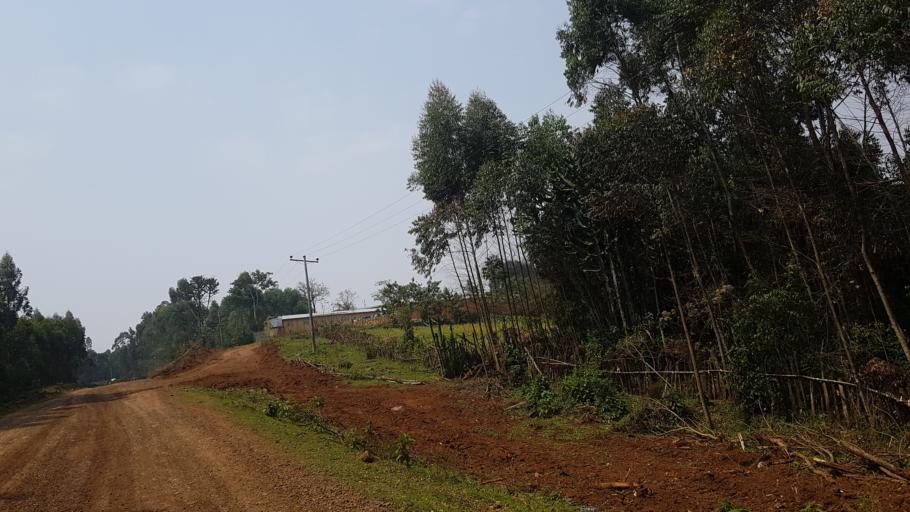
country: ET
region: Oromiya
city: Gore
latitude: 7.7928
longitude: 35.4566
